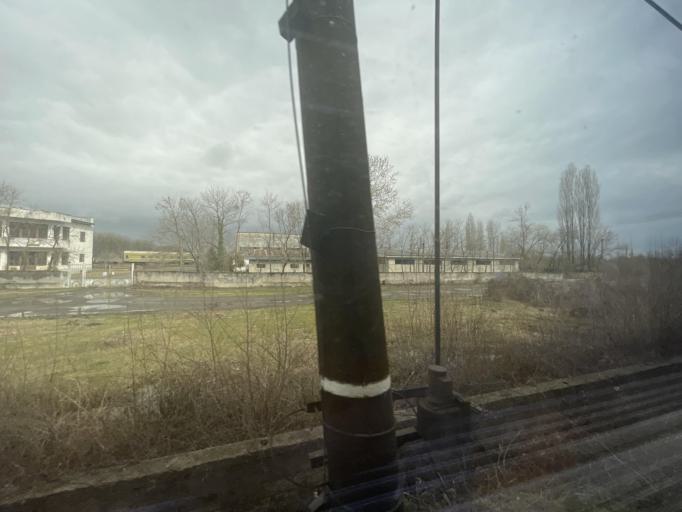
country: GE
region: Guria
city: Lanchkhuti
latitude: 42.0896
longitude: 42.0532
